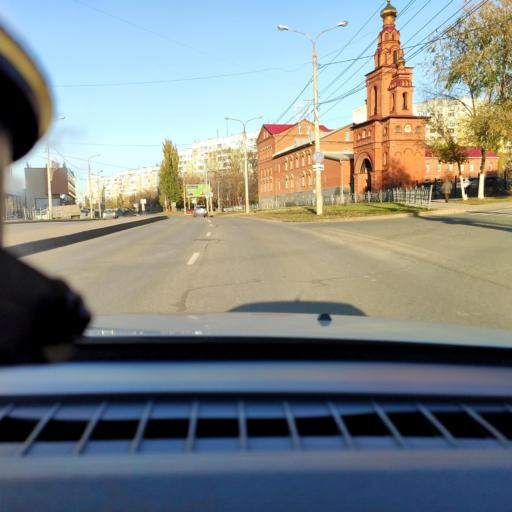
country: RU
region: Samara
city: Samara
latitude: 53.2486
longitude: 50.1989
